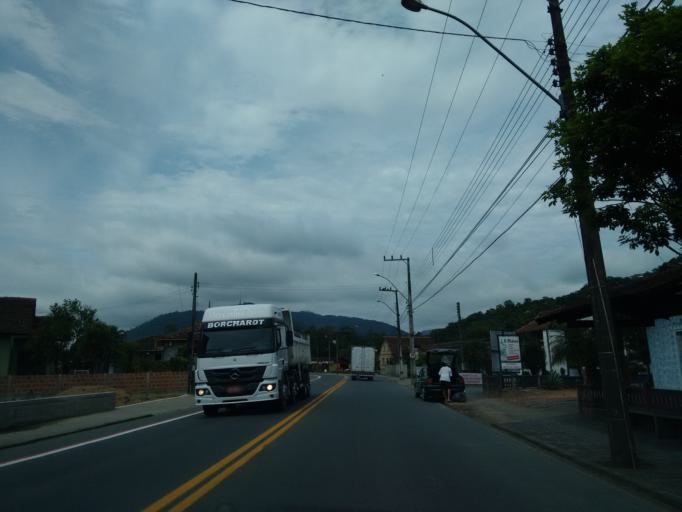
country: BR
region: Santa Catarina
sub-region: Pomerode
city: Pomerode
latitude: -26.7132
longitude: -49.1653
